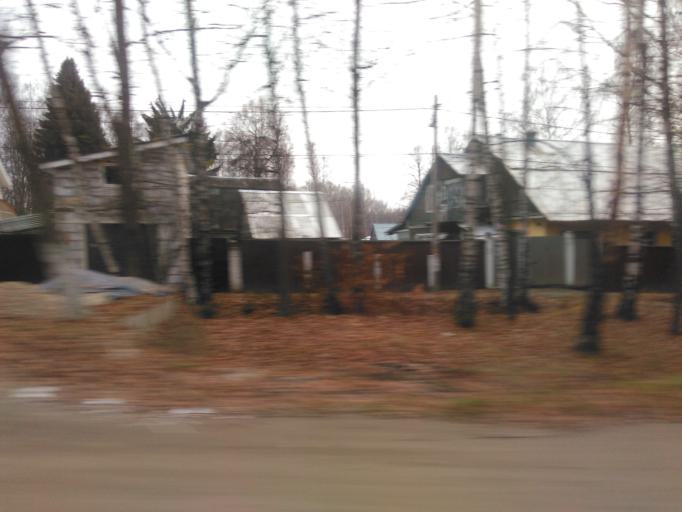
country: RU
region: Moskovskaya
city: Ashukino
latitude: 56.1603
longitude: 37.9508
